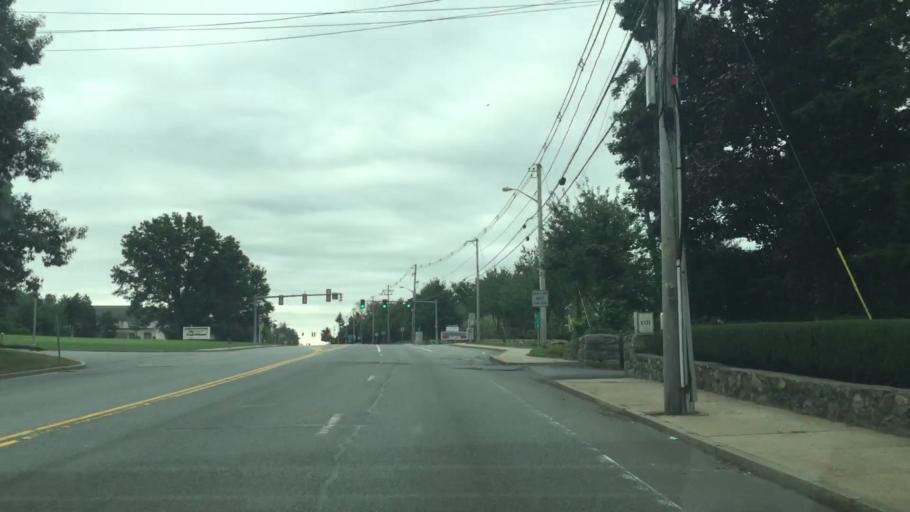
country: US
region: Massachusetts
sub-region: Essex County
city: Andover
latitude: 42.6771
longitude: -71.1312
